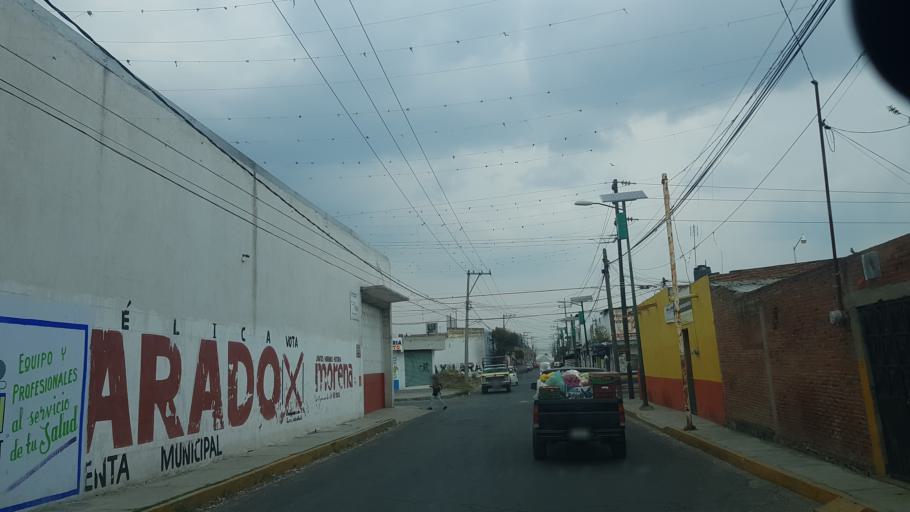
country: MX
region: Puebla
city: Huejotzingo
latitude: 19.1629
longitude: -98.4119
